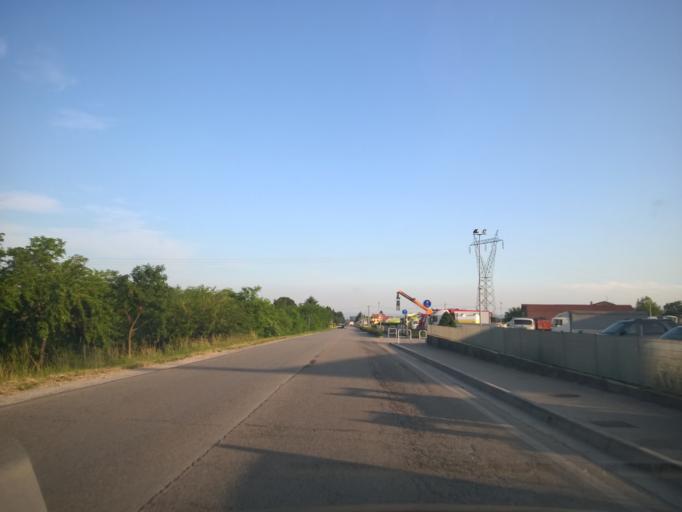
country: IT
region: Veneto
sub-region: Provincia di Vicenza
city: Centrale
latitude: 45.7319
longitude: 11.4647
